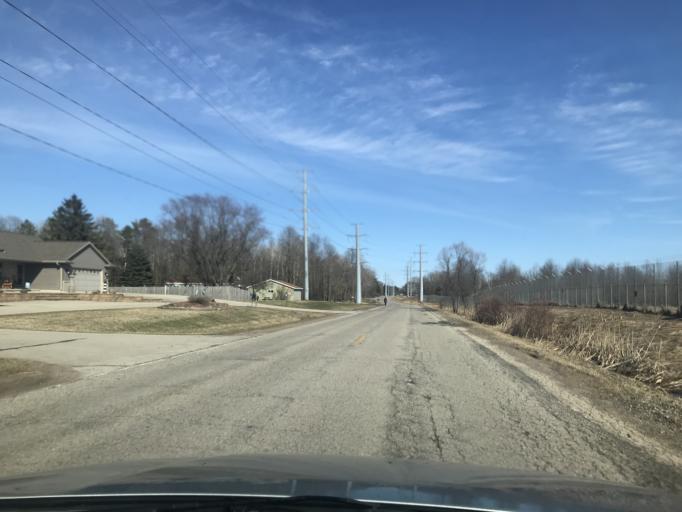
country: US
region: Michigan
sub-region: Menominee County
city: Menominee
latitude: 45.1445
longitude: -87.6300
